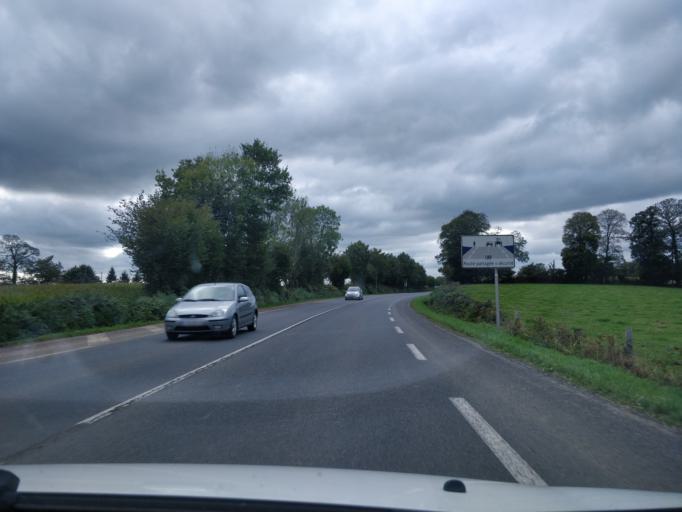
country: FR
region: Lower Normandy
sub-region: Departement du Calvados
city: Saint-Sever-Calvados
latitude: 48.8225
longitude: -1.1092
